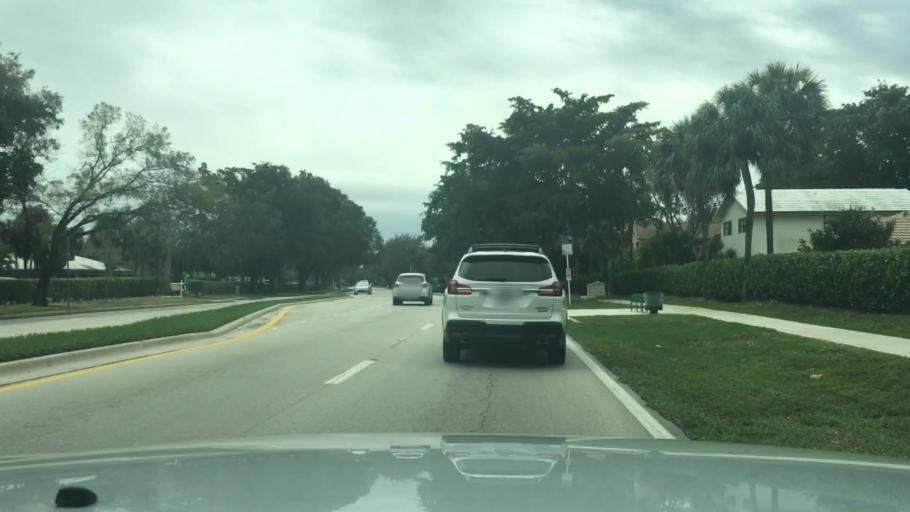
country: US
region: Florida
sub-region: Broward County
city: North Lauderdale
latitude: 26.2464
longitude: -80.2428
